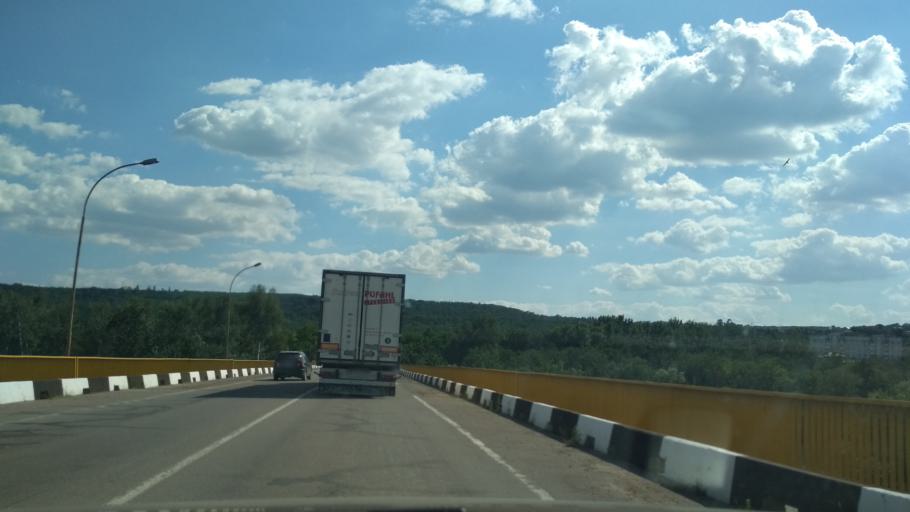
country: MD
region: Chisinau
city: Vadul lui Voda
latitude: 47.0898
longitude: 29.0917
